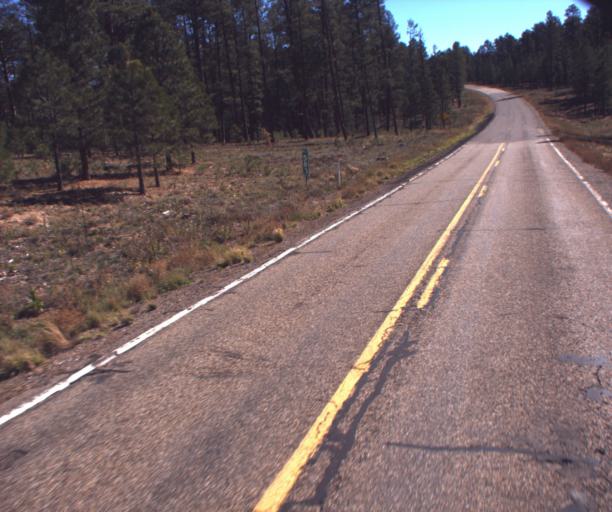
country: US
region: Arizona
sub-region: Coconino County
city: Fredonia
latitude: 36.7460
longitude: -112.2453
